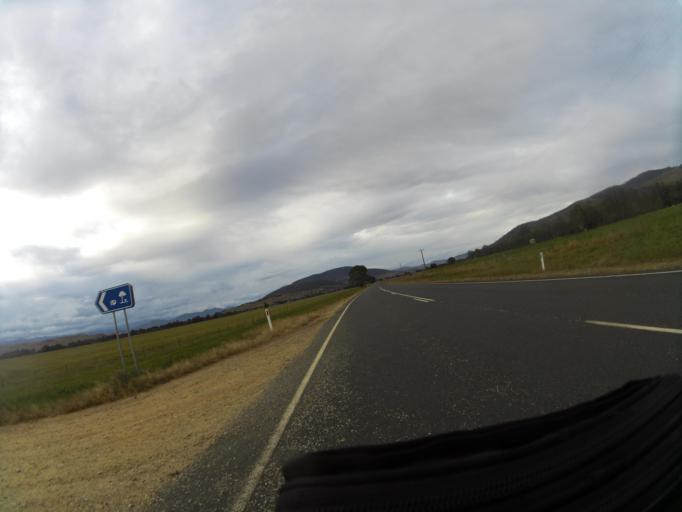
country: AU
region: New South Wales
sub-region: Snowy River
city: Jindabyne
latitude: -36.0945
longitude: 147.9820
